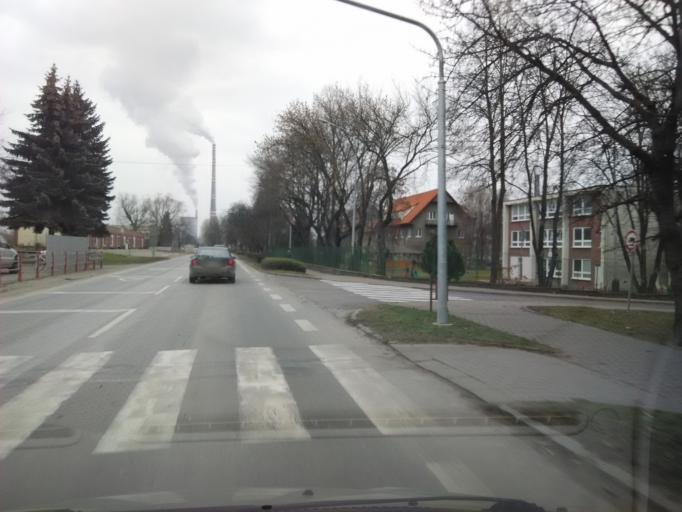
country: SK
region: Nitriansky
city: Novaky
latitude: 48.7133
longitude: 18.5383
